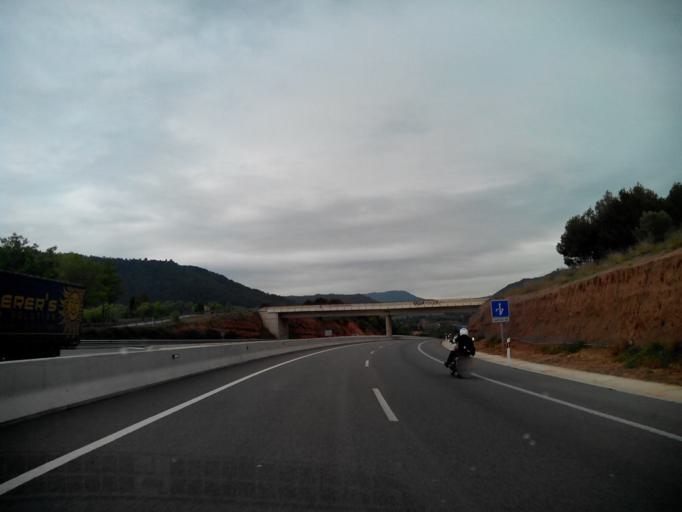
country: ES
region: Catalonia
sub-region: Provincia de Barcelona
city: Sant Joan de Vilatorrada
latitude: 41.7304
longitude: 1.7637
